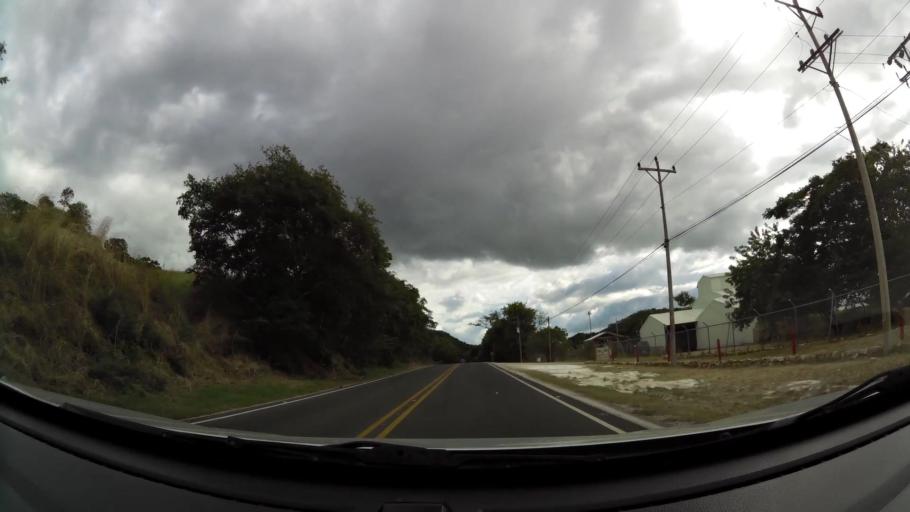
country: CR
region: Guanacaste
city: Nandayure
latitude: 10.2377
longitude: -85.2202
